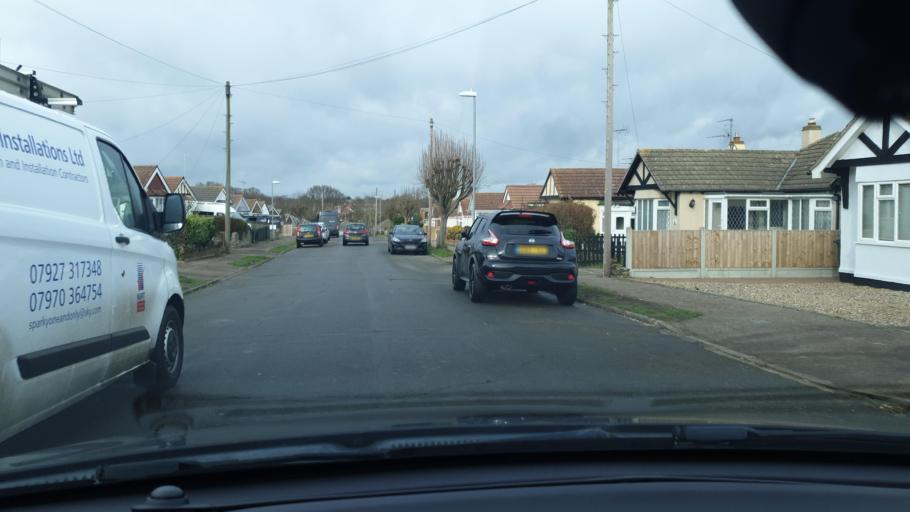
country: GB
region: England
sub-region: Essex
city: Clacton-on-Sea
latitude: 51.8032
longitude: 1.1794
